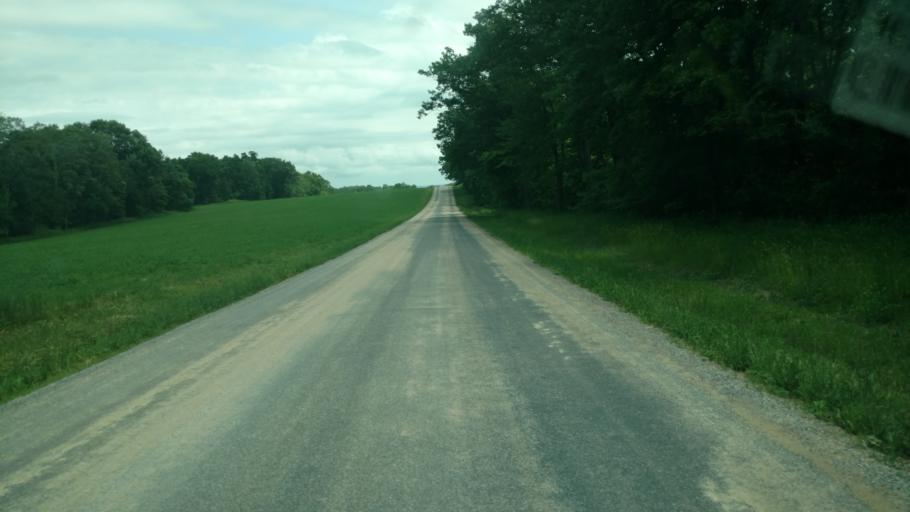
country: US
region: Wisconsin
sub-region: Monroe County
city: Cashton
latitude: 43.6920
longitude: -90.6578
